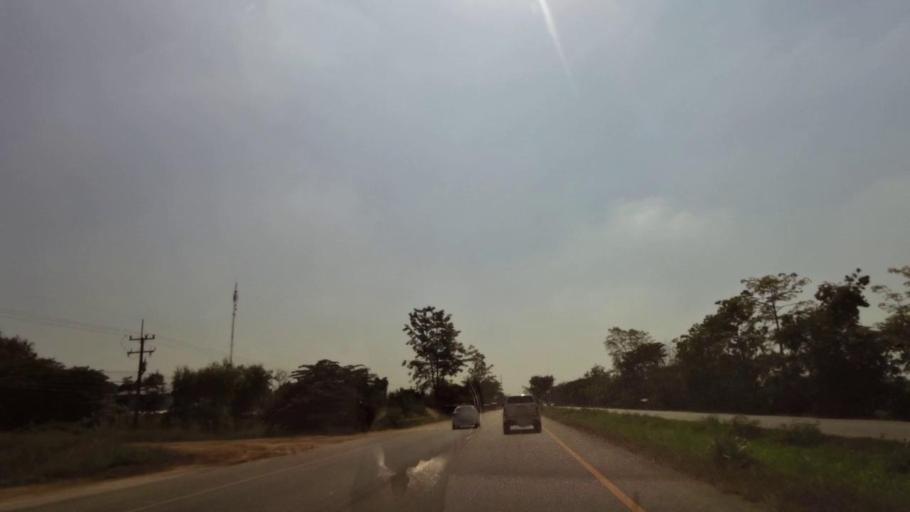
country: TH
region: Phichit
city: Wachira Barami
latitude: 16.4214
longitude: 100.1441
